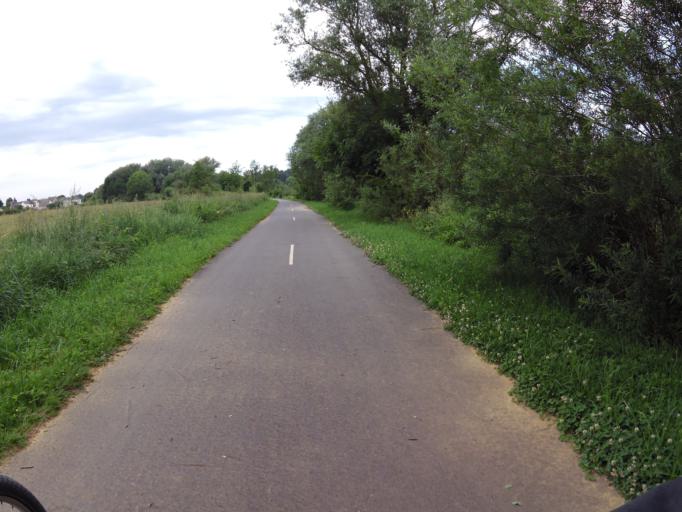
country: FR
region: Champagne-Ardenne
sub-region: Departement des Ardennes
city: Floing
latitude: 49.7125
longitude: 4.9210
